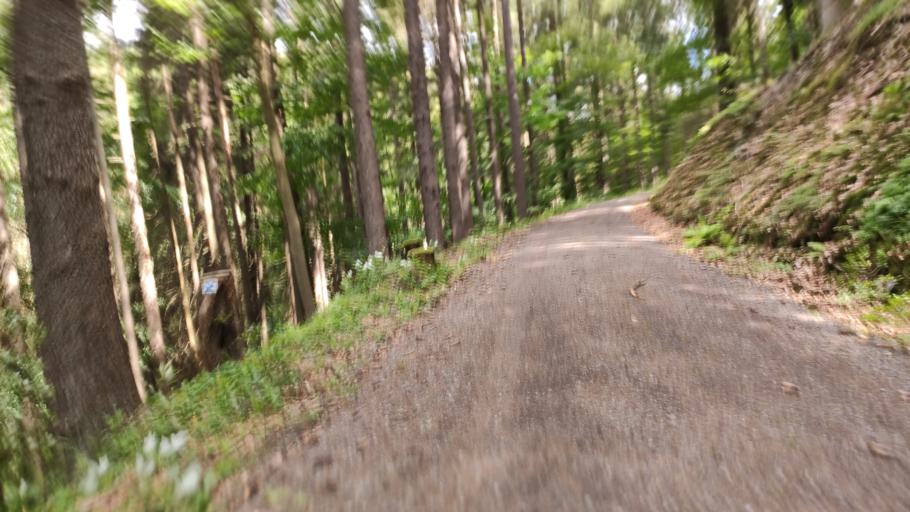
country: DE
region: Bavaria
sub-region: Upper Franconia
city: Tschirn
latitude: 50.3805
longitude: 11.4663
